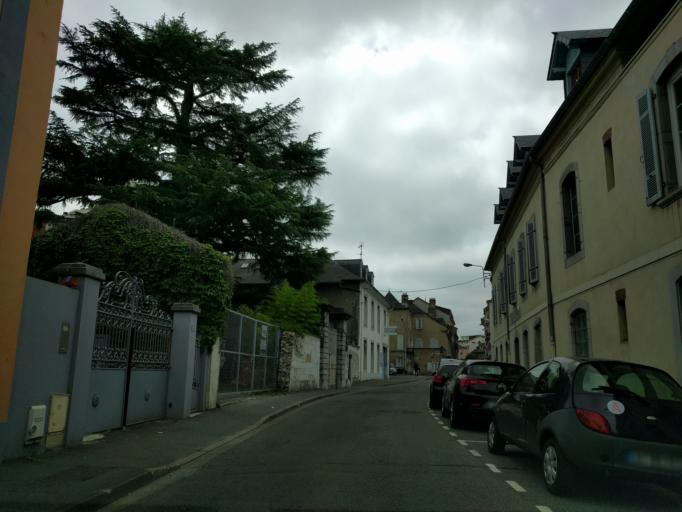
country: FR
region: Midi-Pyrenees
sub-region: Departement des Hautes-Pyrenees
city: Tarbes
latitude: 43.2353
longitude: 0.0741
